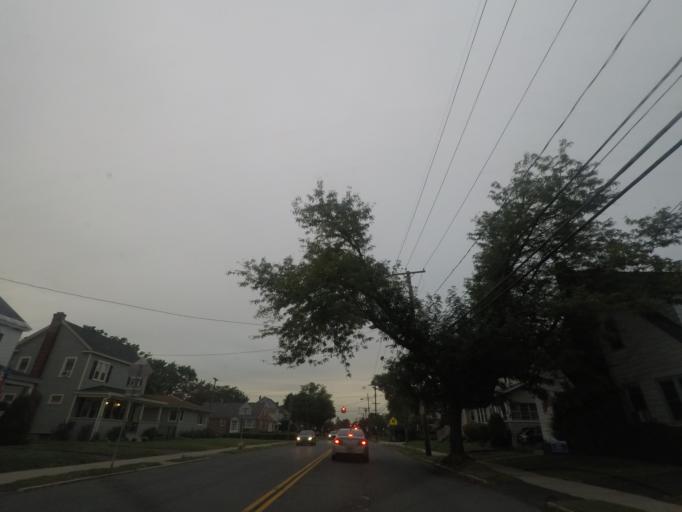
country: US
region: New York
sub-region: Albany County
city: Albany
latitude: 42.6430
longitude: -73.7907
